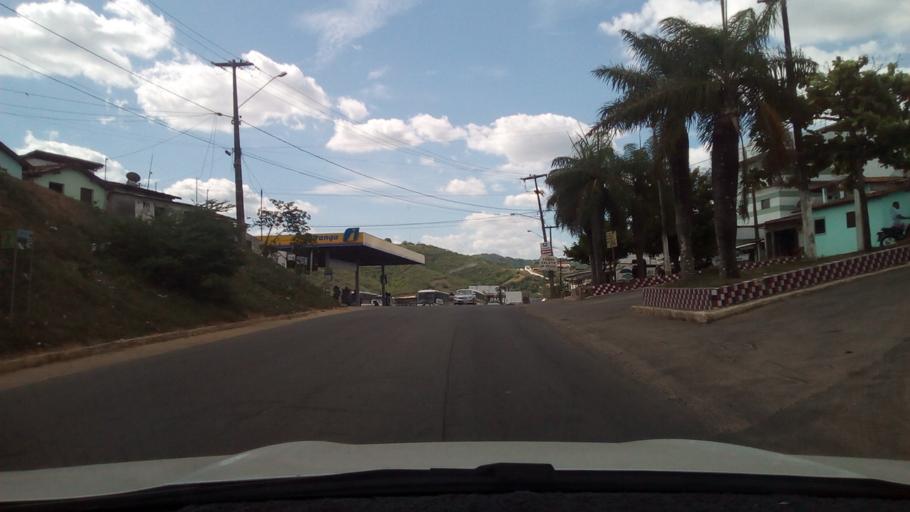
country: BR
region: Paraiba
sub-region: Guarabira
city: Guarabira
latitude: -6.8639
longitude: -35.4943
